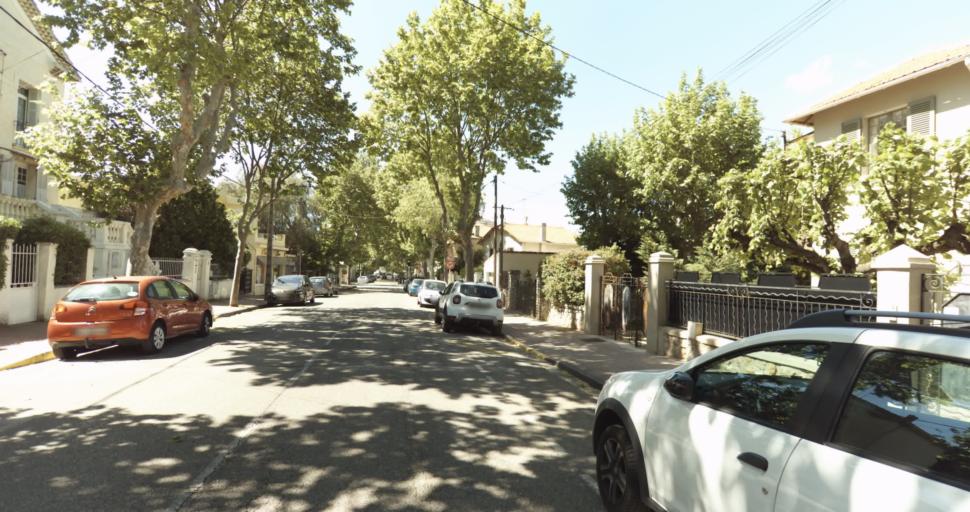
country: FR
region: Provence-Alpes-Cote d'Azur
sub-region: Departement du Var
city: Toulon
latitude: 43.1135
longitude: 5.9478
